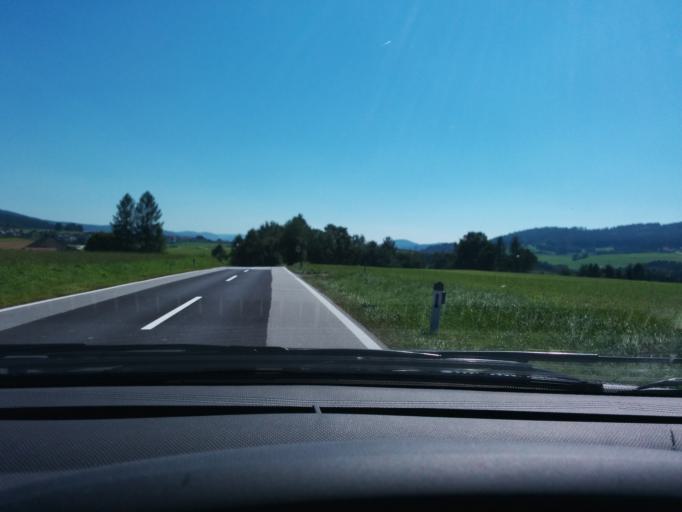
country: AT
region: Upper Austria
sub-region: Politischer Bezirk Rohrbach
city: Ulrichsberg
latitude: 48.6691
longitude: 13.9306
